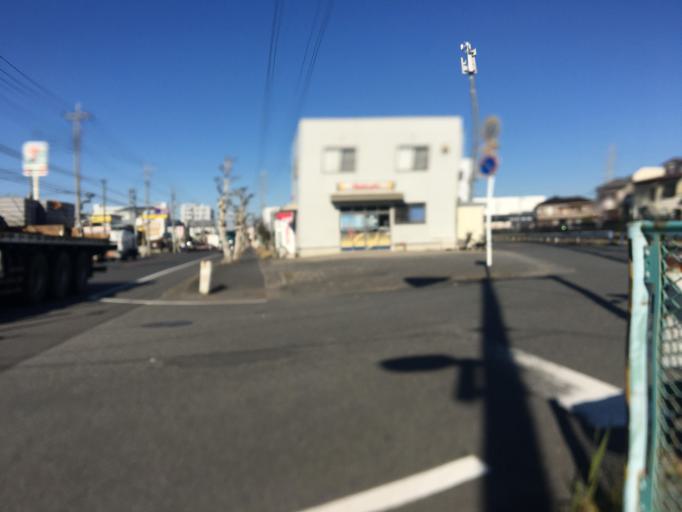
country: JP
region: Saitama
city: Yashio-shi
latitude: 35.8342
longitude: 139.8314
